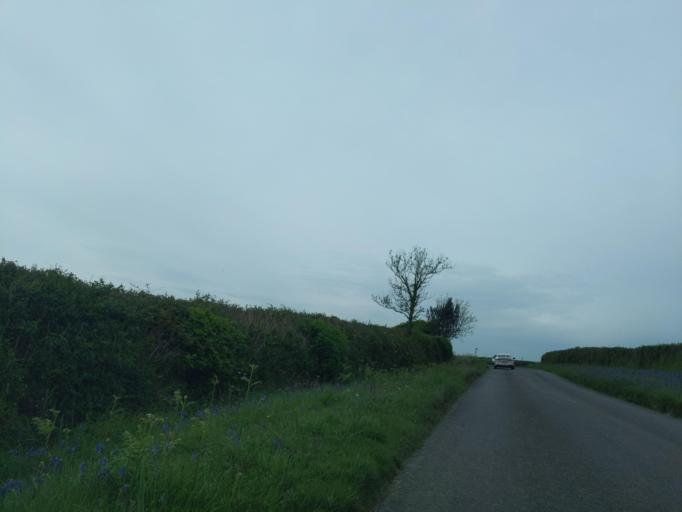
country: GB
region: England
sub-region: Devon
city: Plympton
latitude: 50.4284
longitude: -4.0497
